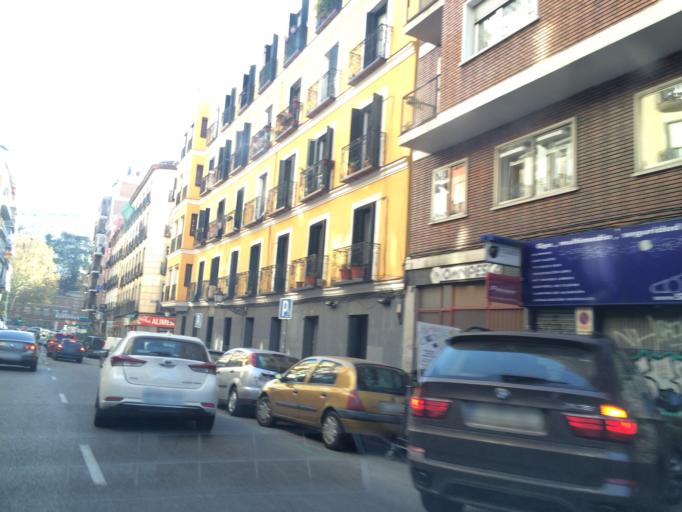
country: ES
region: Madrid
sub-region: Provincia de Madrid
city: City Center
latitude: 40.4217
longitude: -3.7162
